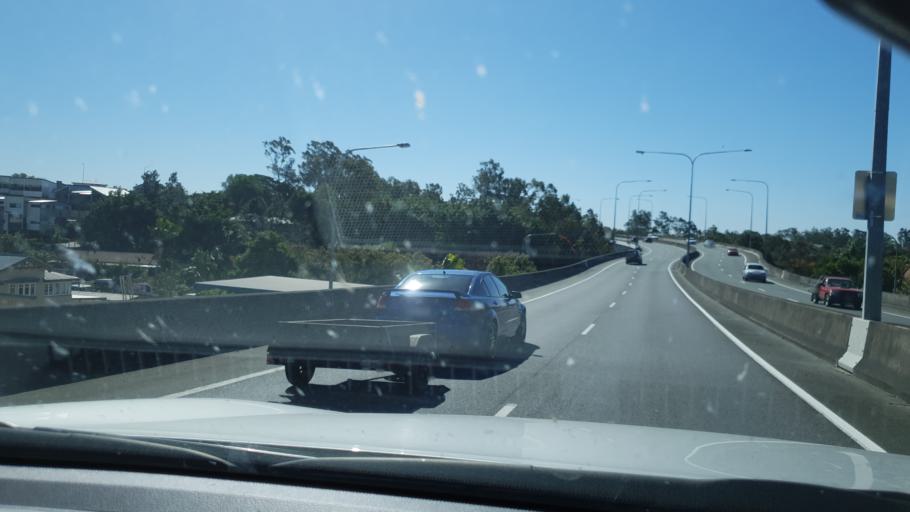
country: AU
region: Queensland
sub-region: Brisbane
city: Everton Park
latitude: -27.3878
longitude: 152.9848
